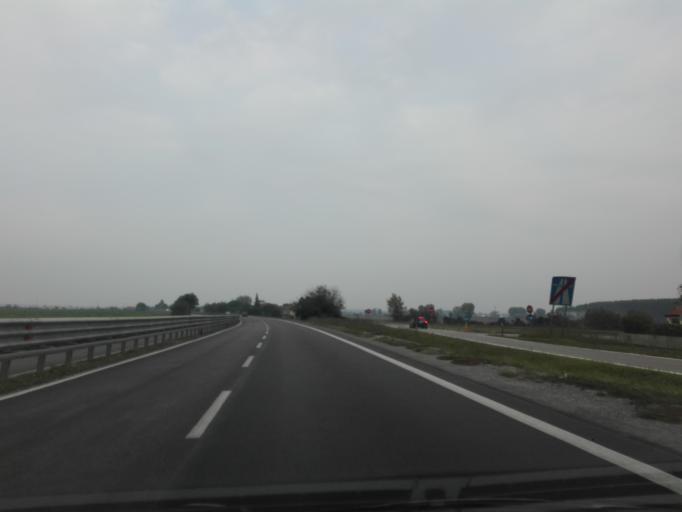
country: IT
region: Veneto
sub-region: Provincia di Verona
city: Vallese
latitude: 45.3185
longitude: 11.1039
